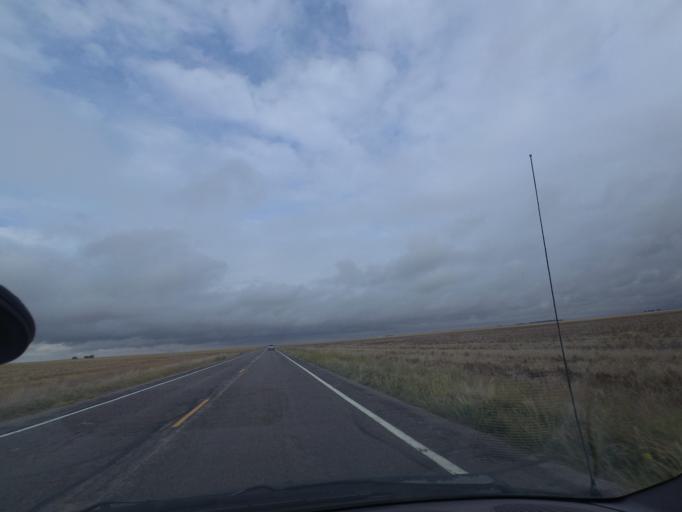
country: US
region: Colorado
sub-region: Washington County
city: Akron
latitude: 39.6991
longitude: -103.0121
